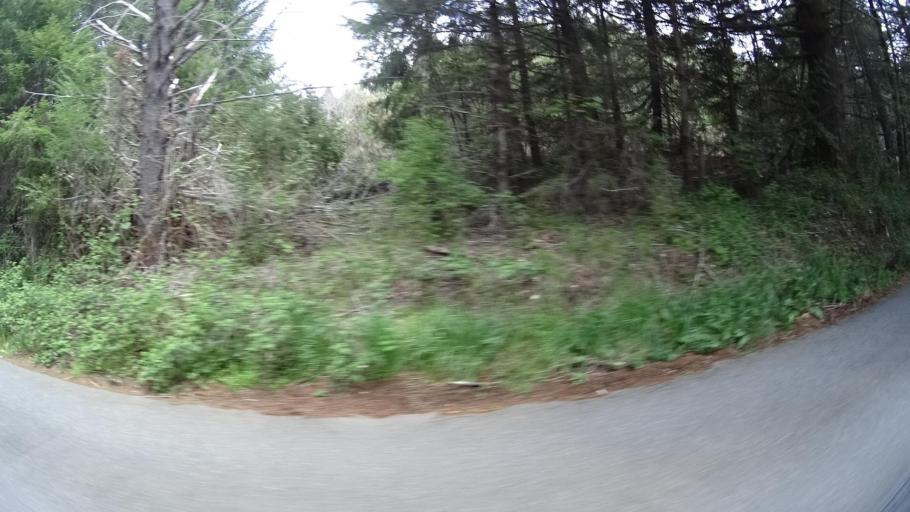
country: US
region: California
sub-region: Humboldt County
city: Redway
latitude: 40.0135
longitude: -123.9334
